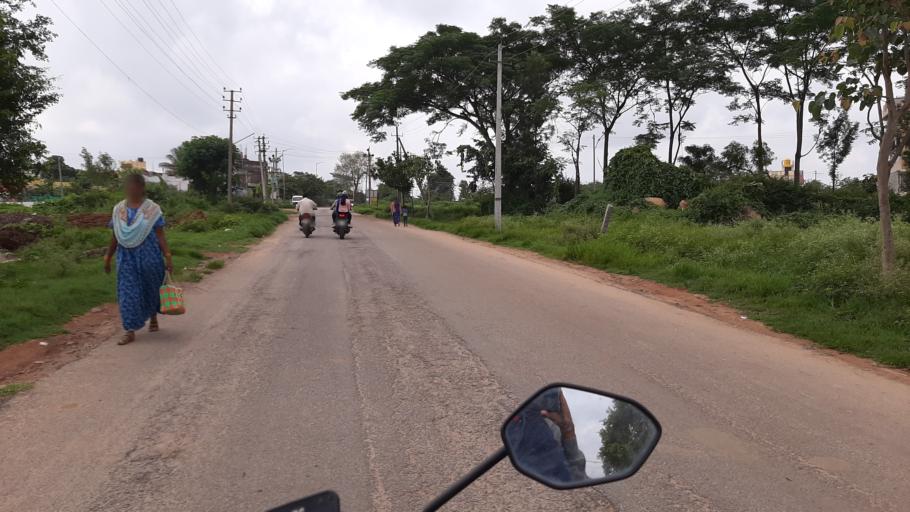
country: IN
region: Karnataka
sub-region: Ramanagara
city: Magadi
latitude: 12.9500
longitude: 77.2378
